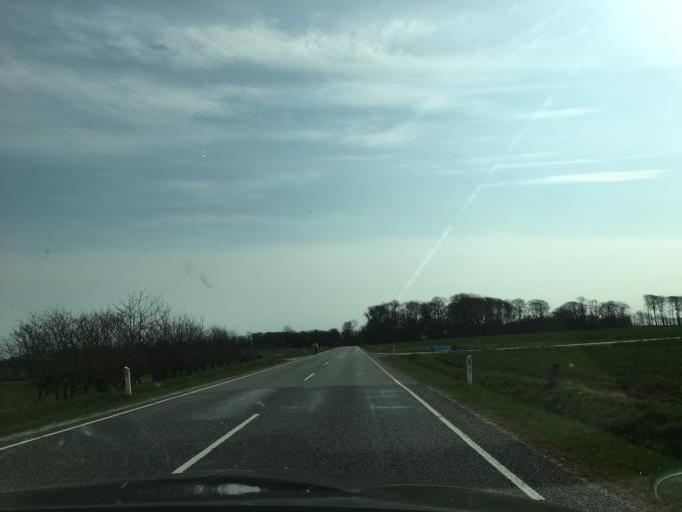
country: DK
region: South Denmark
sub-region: Vejen Kommune
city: Brorup
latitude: 55.4946
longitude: 9.0533
